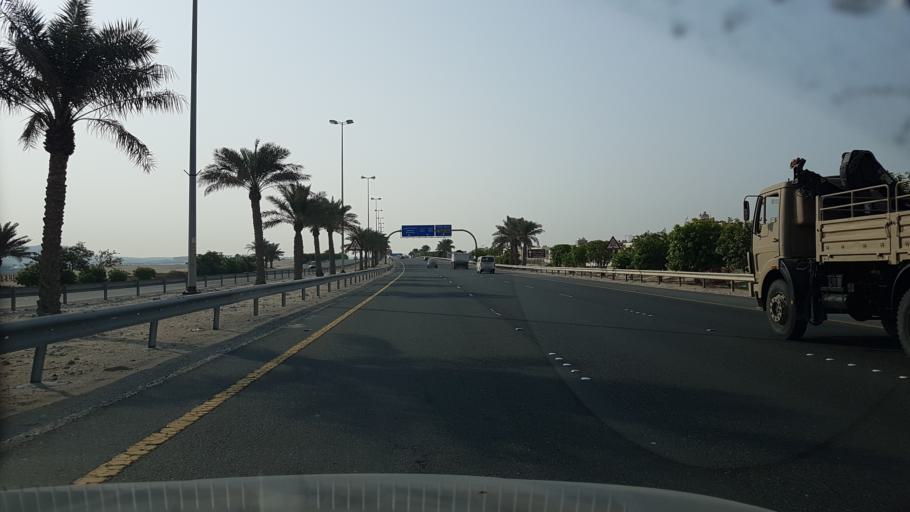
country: BH
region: Central Governorate
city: Dar Kulayb
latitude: 26.0703
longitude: 50.5151
